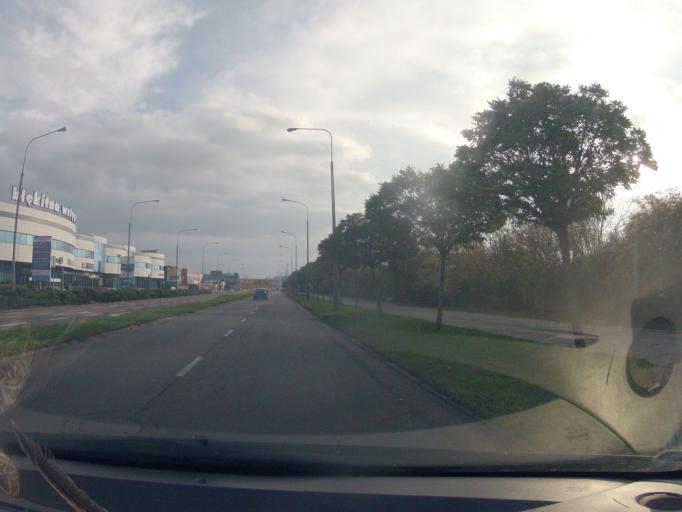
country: PL
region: Opole Voivodeship
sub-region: Powiat opolski
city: Opole
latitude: 50.6720
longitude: 17.9502
